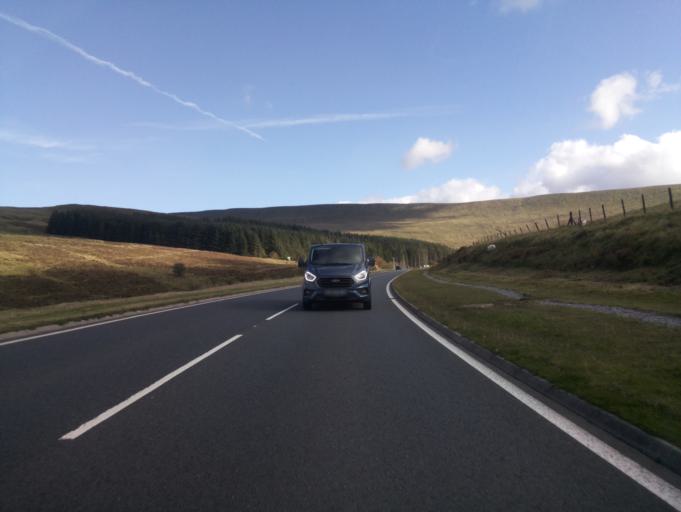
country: GB
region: Wales
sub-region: Sir Powys
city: Brecon
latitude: 51.8729
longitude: -3.4840
